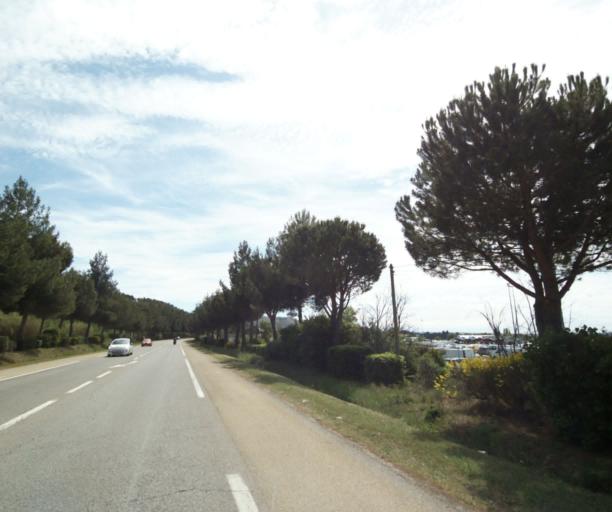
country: FR
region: Provence-Alpes-Cote d'Azur
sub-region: Departement des Bouches-du-Rhone
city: Rognac
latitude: 43.4994
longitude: 5.2274
